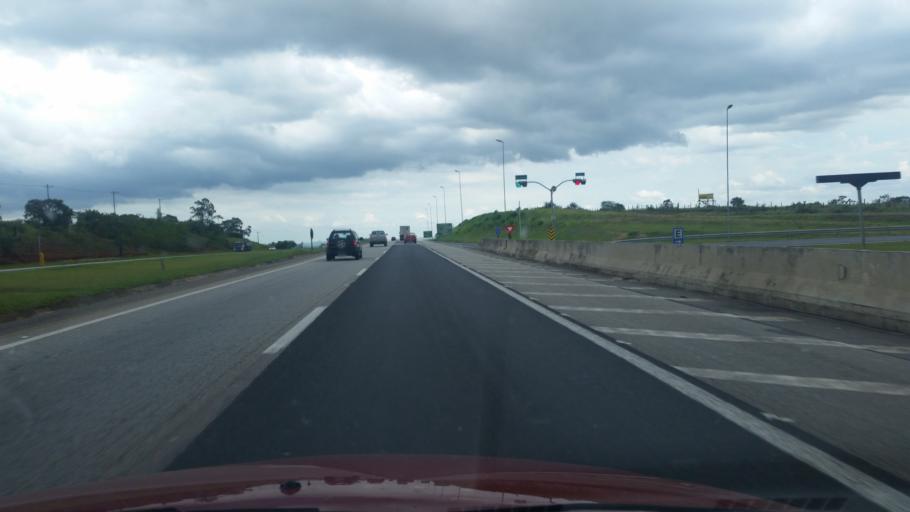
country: BR
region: Sao Paulo
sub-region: Sorocaba
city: Sorocaba
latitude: -23.3597
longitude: -47.4929
